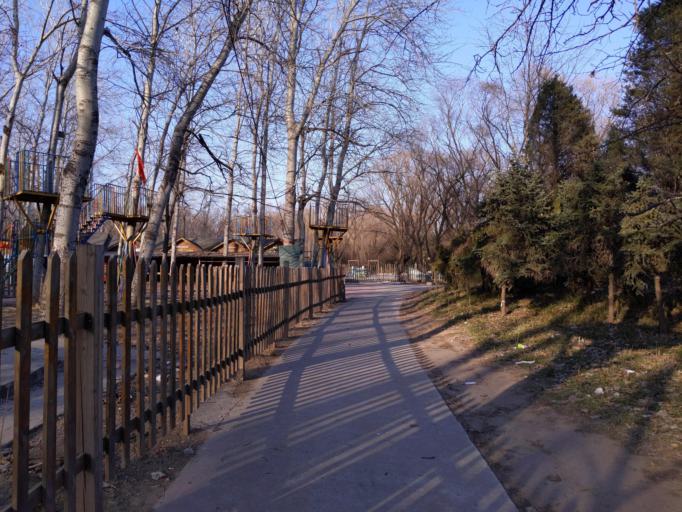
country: CN
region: Henan Sheng
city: Puyang
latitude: 35.7777
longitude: 114.9605
